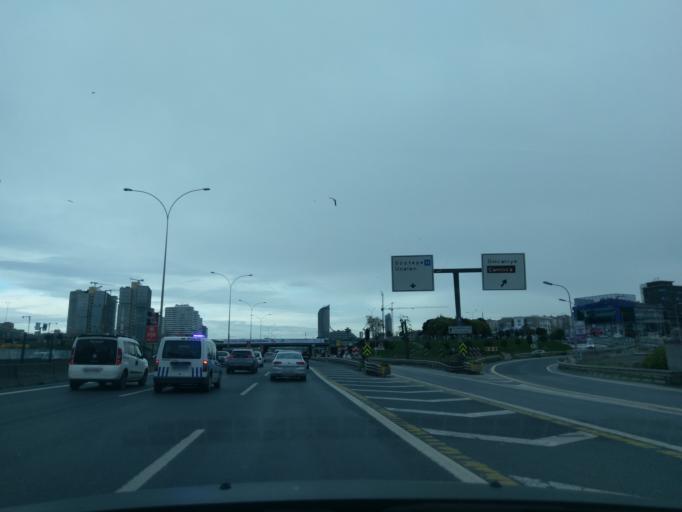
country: TR
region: Istanbul
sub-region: Atasehir
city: Atasehir
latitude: 40.9917
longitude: 29.0759
